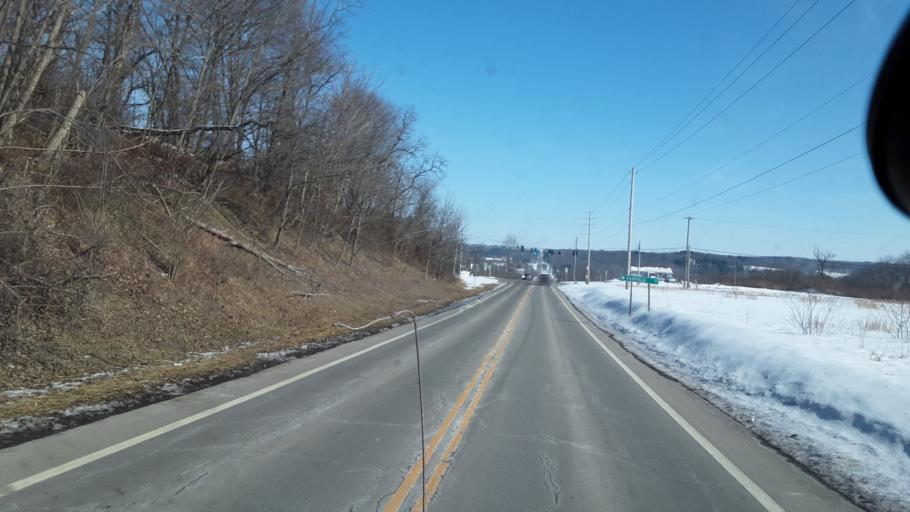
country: US
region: Ohio
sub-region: Columbiana County
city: Salem
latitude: 40.9442
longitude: -80.8391
